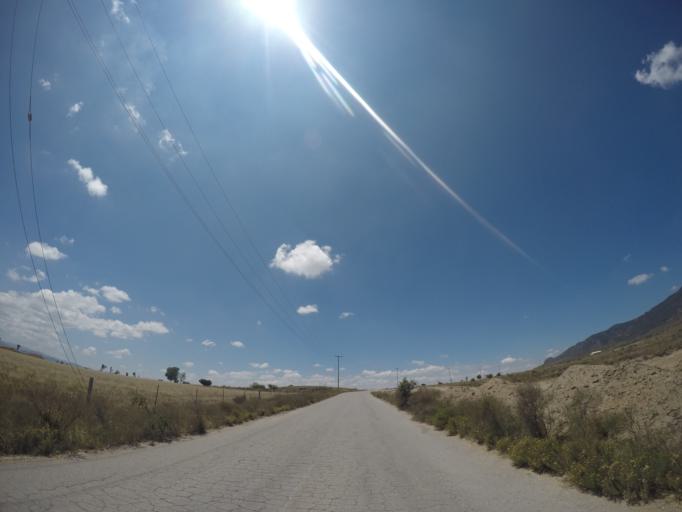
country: MX
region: San Luis Potosi
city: La Pila
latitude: 22.0181
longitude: -100.9088
